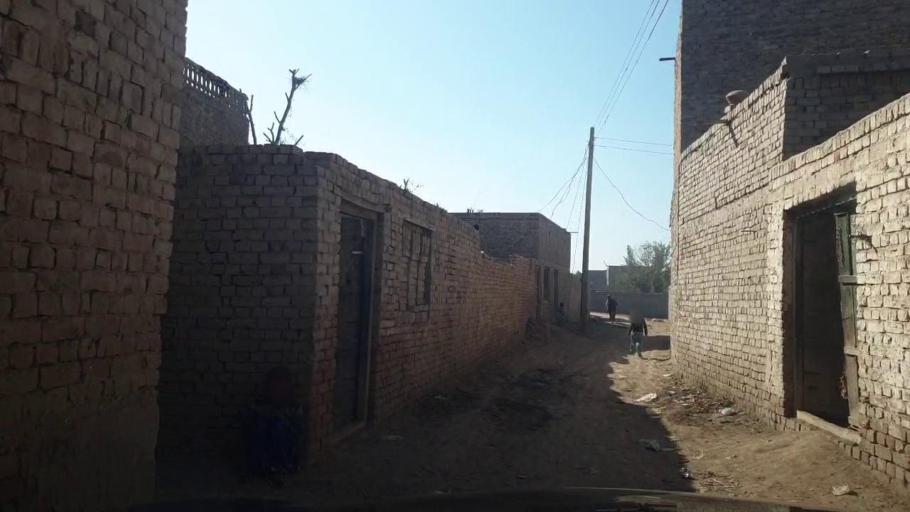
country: PK
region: Sindh
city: Ghotki
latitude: 28.0007
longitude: 69.3276
